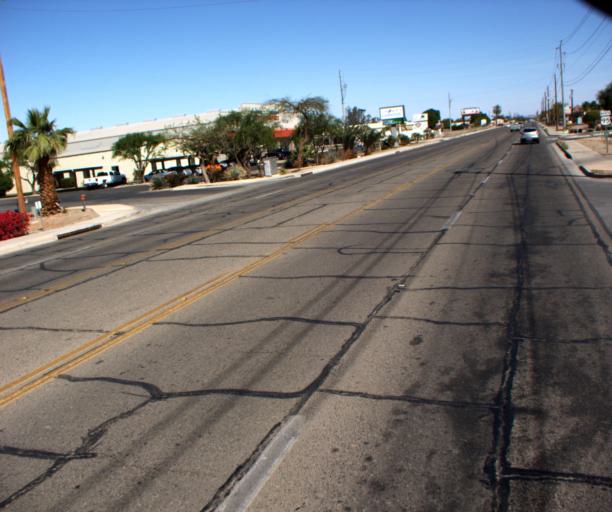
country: US
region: Arizona
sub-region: Yuma County
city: Yuma
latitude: 32.6710
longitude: -114.6501
